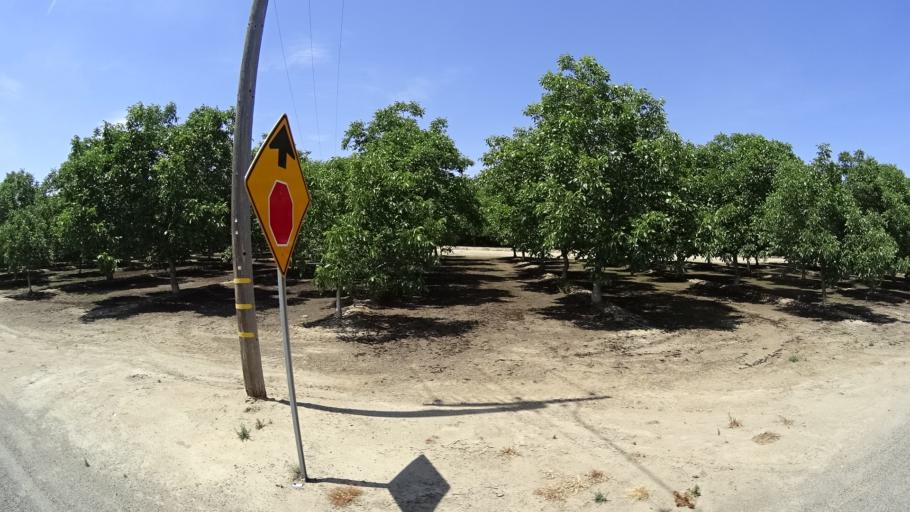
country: US
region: California
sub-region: Kings County
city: Home Garden
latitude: 36.2712
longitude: -119.6728
